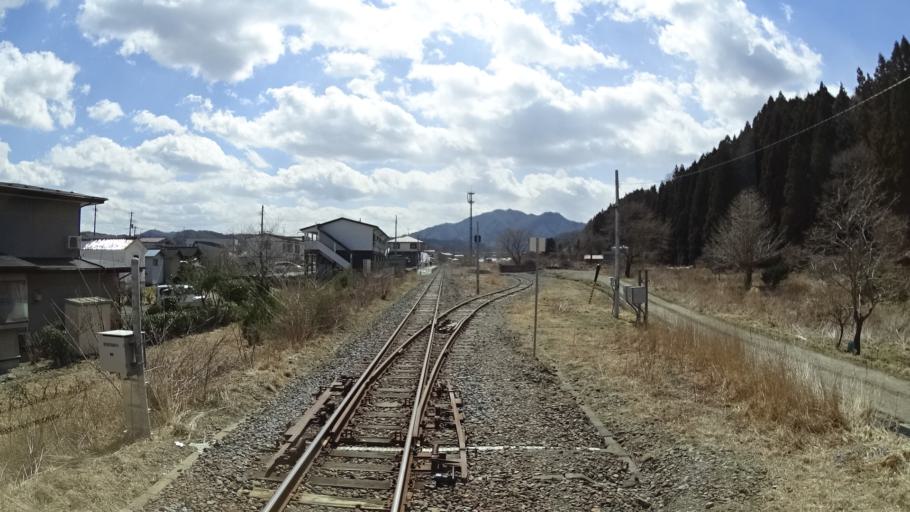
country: JP
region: Iwate
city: Yamada
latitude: 39.5354
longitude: 141.9248
